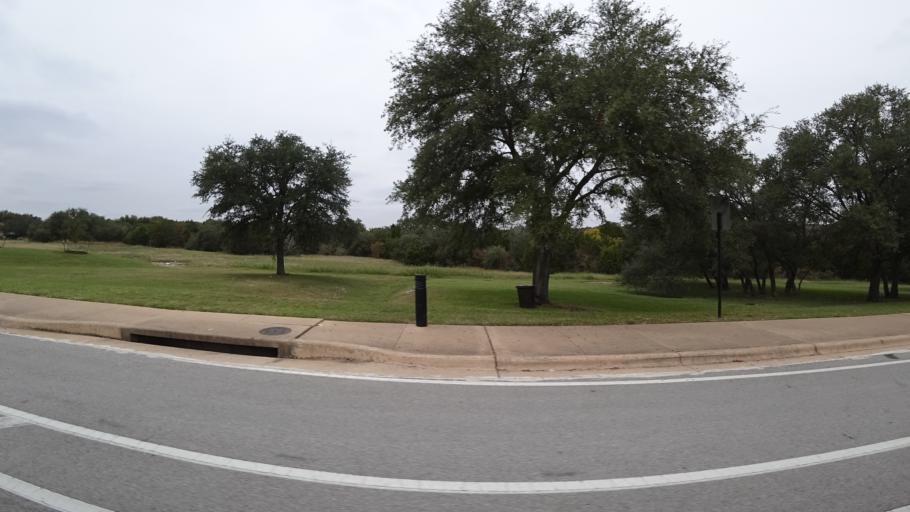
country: US
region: Texas
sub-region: Travis County
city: Shady Hollow
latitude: 30.1954
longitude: -97.8814
